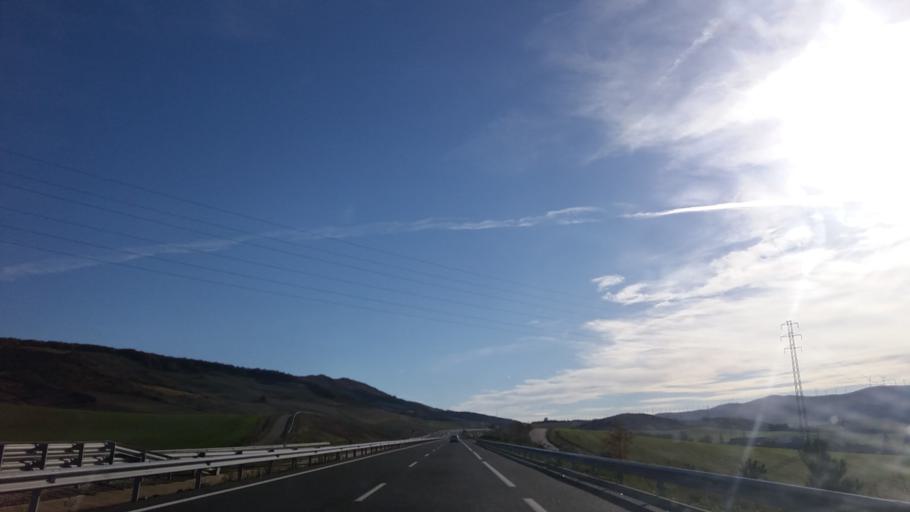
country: ES
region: Navarre
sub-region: Provincia de Navarra
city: Monreal
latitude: 42.7104
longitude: -1.5055
